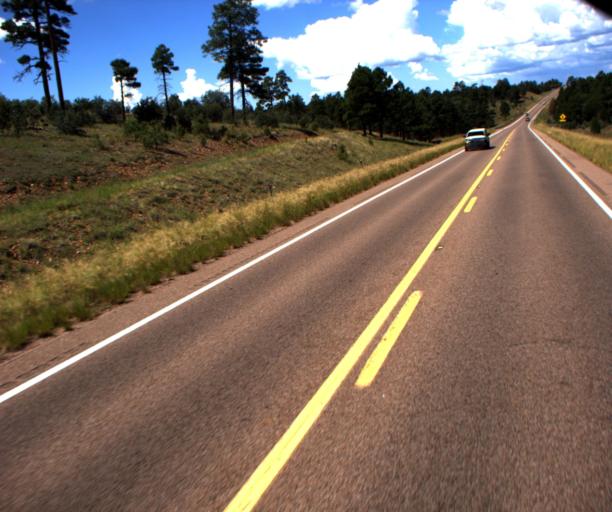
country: US
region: Arizona
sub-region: Navajo County
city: Heber-Overgaard
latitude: 34.3676
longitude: -110.3827
